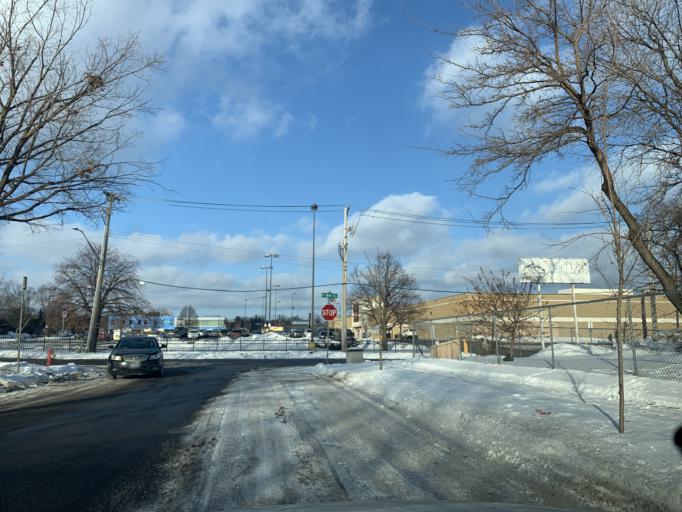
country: US
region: Minnesota
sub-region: Hennepin County
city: Minneapolis
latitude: 44.9971
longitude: -93.2895
